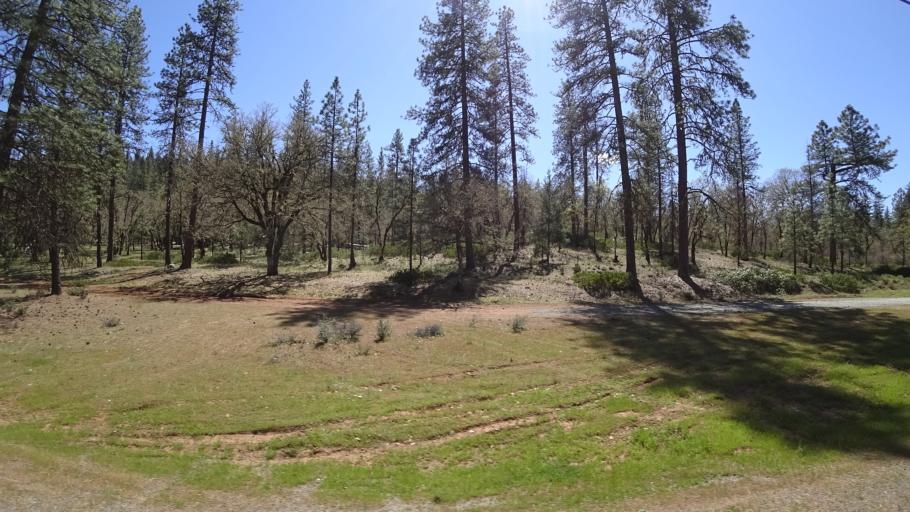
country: US
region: California
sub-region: Trinity County
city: Weaverville
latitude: 40.7536
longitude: -122.9064
